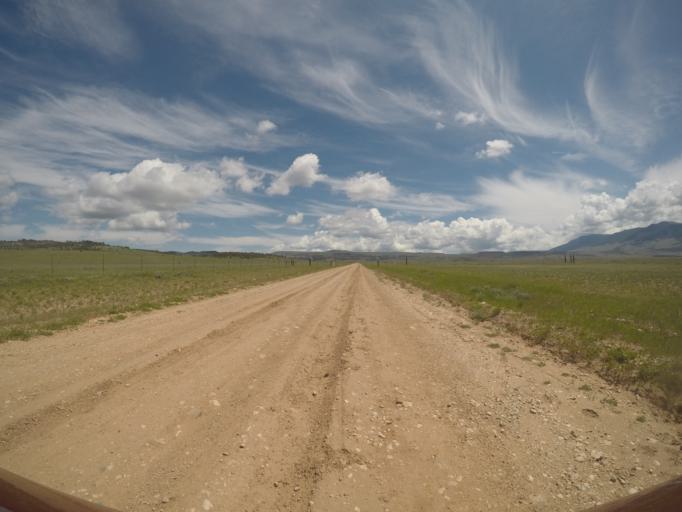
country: US
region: Montana
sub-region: Yellowstone County
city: Laurel
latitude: 45.2343
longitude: -108.6898
